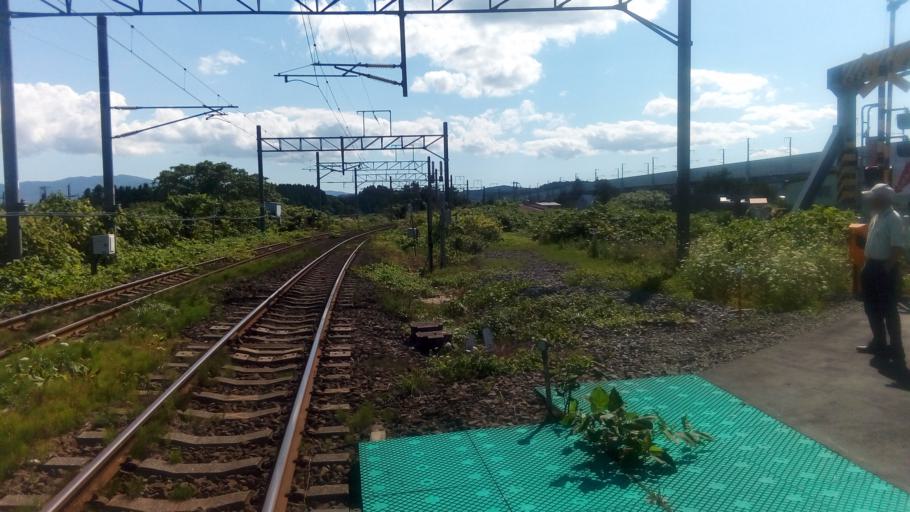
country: JP
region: Hokkaido
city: Kamiiso
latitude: 41.6726
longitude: 140.4290
